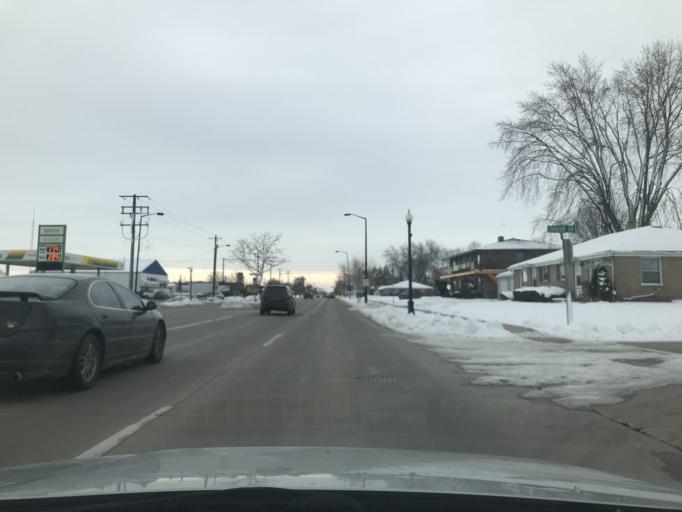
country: US
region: Wisconsin
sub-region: Brown County
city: Ashwaubenon
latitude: 44.4980
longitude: -88.0594
